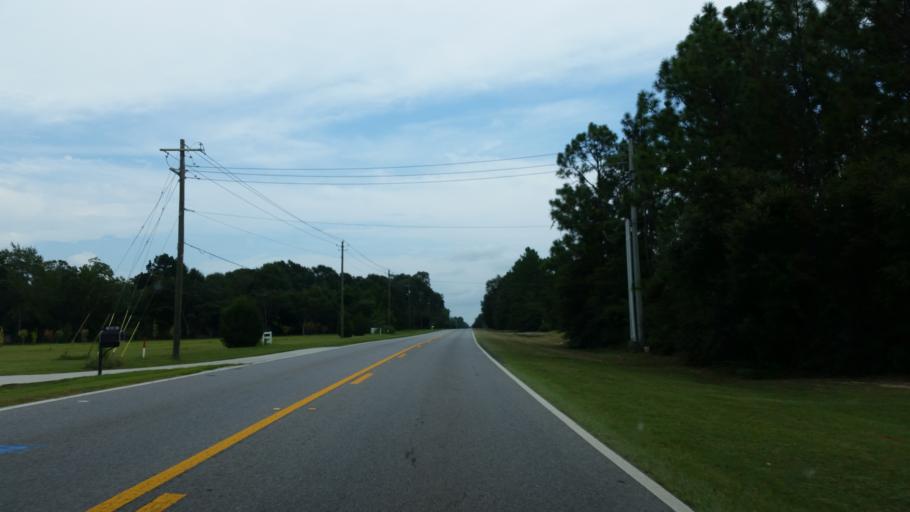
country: US
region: Florida
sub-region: Santa Rosa County
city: Wallace
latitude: 30.6594
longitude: -87.1950
